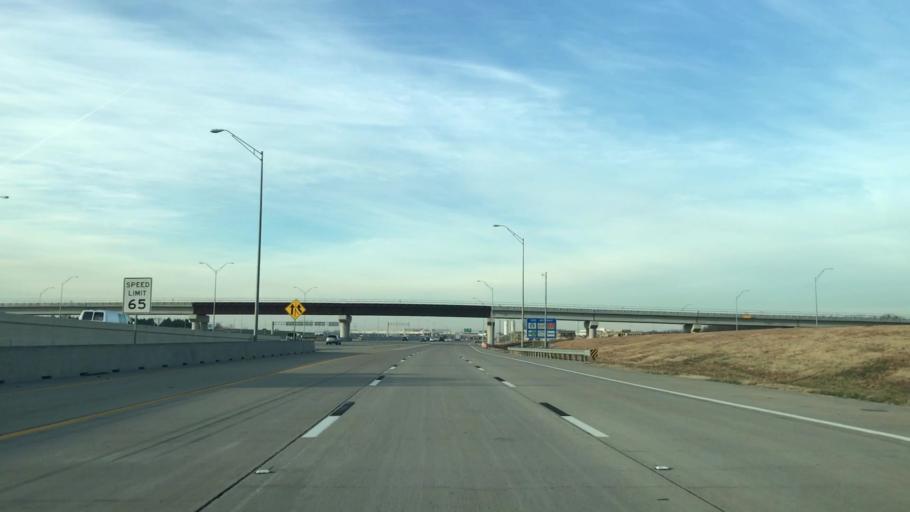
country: US
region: Texas
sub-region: Tarrant County
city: Grapevine
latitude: 32.9307
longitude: -97.0481
